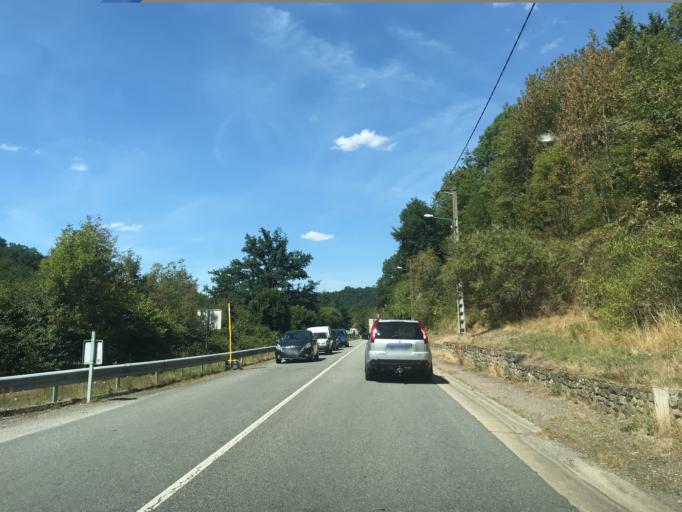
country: FR
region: Limousin
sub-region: Departement de la Creuse
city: Aubusson
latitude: 45.9195
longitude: 2.1933
